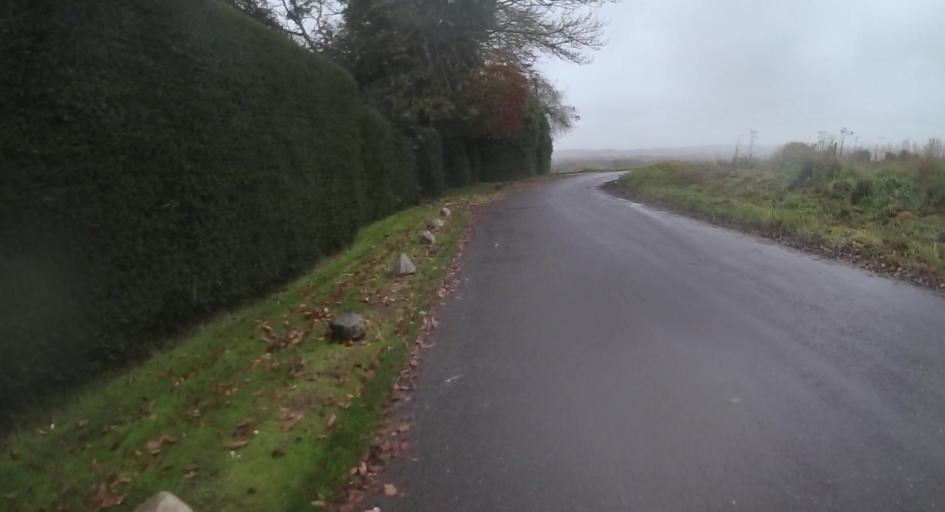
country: GB
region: England
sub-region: Hampshire
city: Kingsley
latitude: 51.1682
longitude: -0.9003
